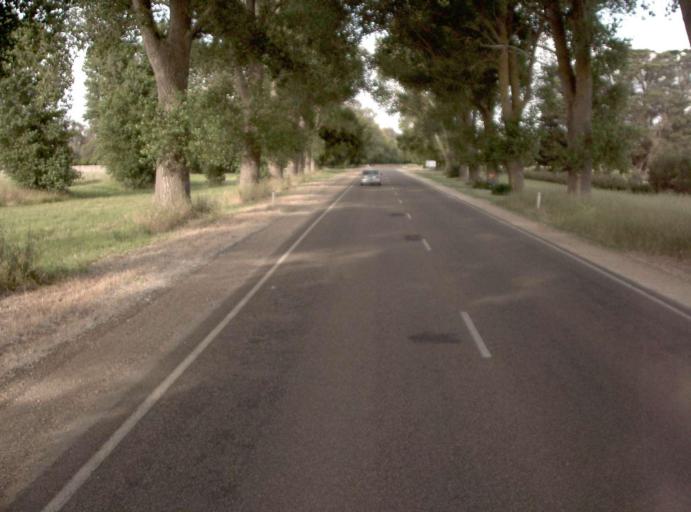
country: AU
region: Victoria
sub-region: Wellington
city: Heyfield
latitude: -37.9677
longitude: 146.9595
